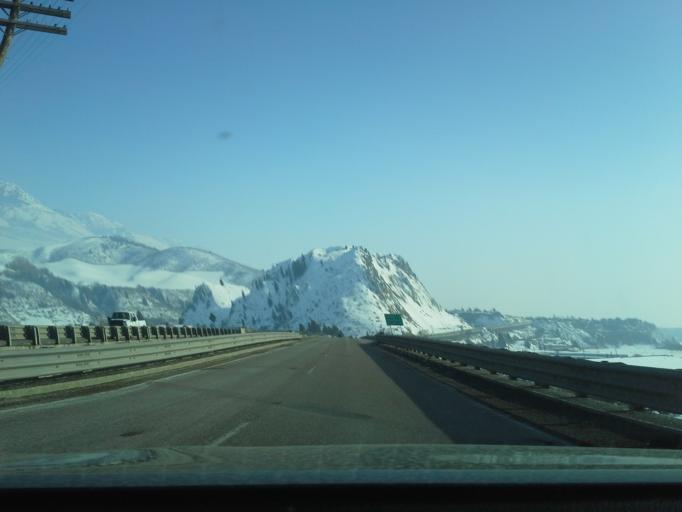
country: US
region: Idaho
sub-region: Bannock County
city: Pocatello
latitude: 42.7871
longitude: -112.2340
